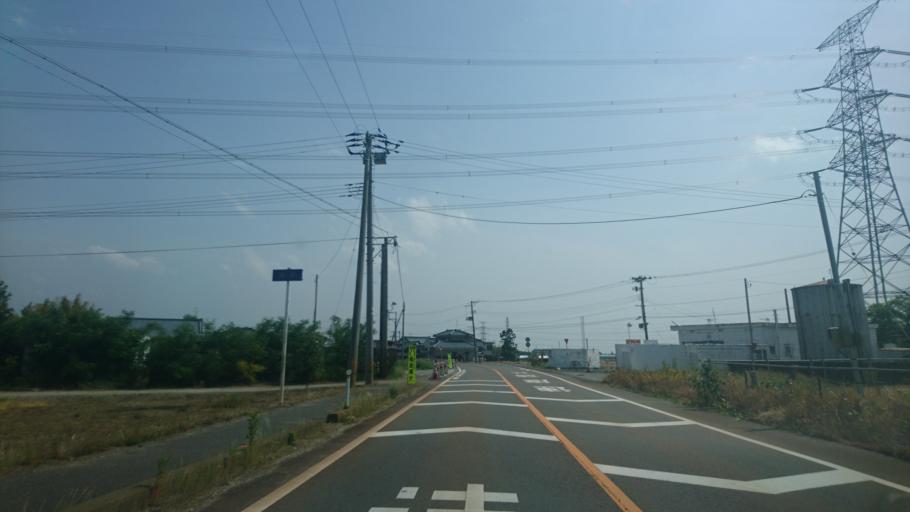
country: JP
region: Niigata
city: Shibata
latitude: 37.9862
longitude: 139.2929
